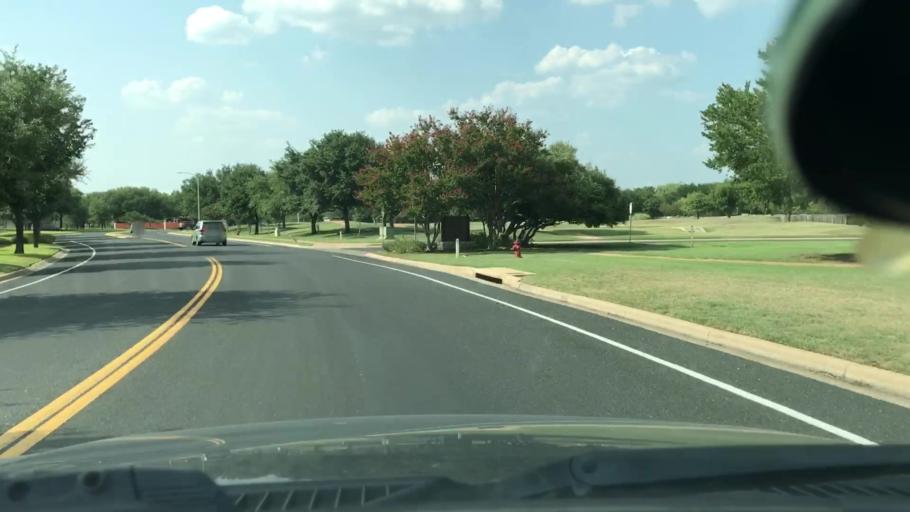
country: US
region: Texas
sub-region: Williamson County
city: Leander
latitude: 30.5438
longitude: -97.8351
